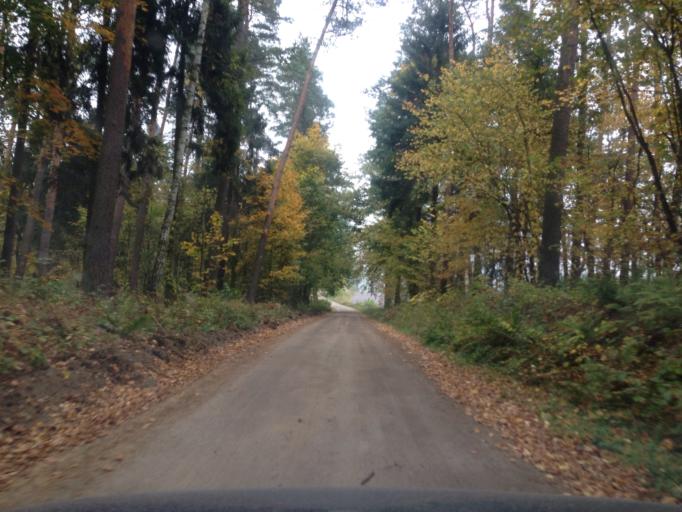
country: PL
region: Kujawsko-Pomorskie
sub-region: Powiat brodnicki
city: Bartniczka
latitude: 53.2663
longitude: 19.5815
